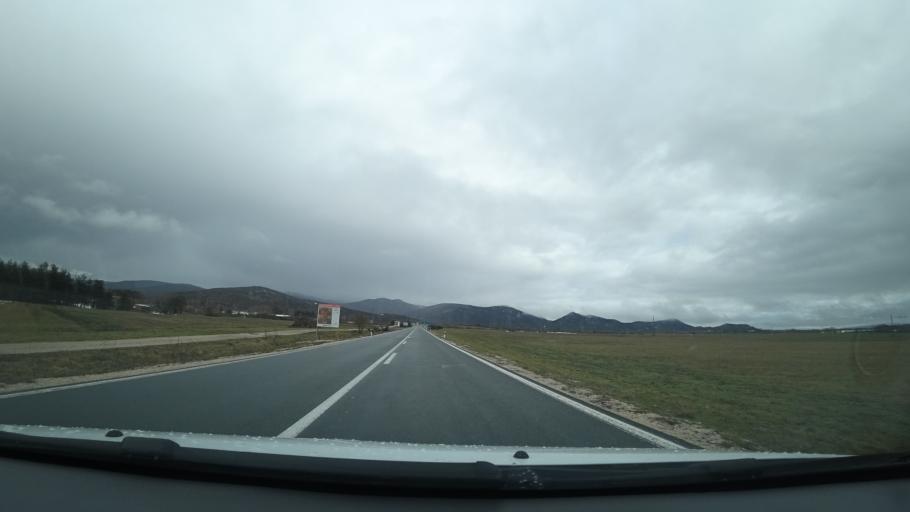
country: HR
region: Licko-Senjska
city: Gospic
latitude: 44.5745
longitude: 15.4143
